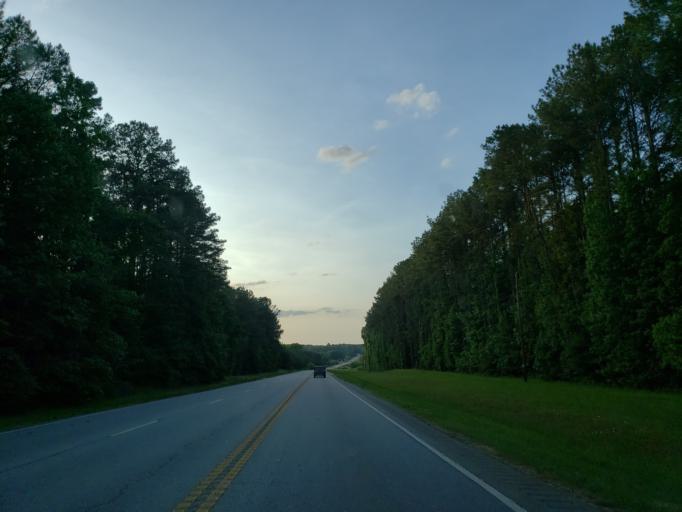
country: US
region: Georgia
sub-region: Coweta County
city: Newnan
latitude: 33.4696
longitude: -84.8967
